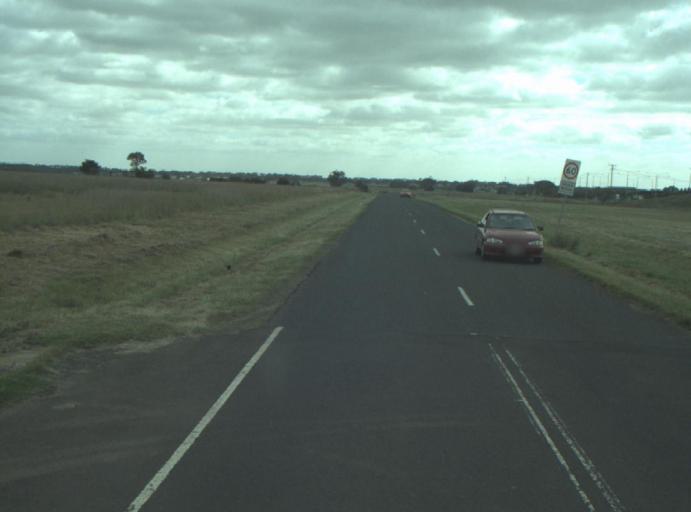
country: AU
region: Victoria
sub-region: Greater Geelong
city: Lara
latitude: -38.0544
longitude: 144.3921
